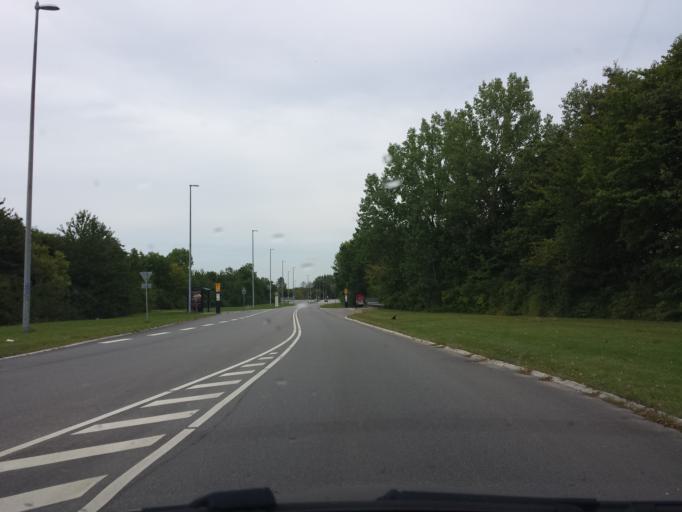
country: DK
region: Capital Region
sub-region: Hoje-Taastrup Kommune
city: Taastrup
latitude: 55.6517
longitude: 12.2664
